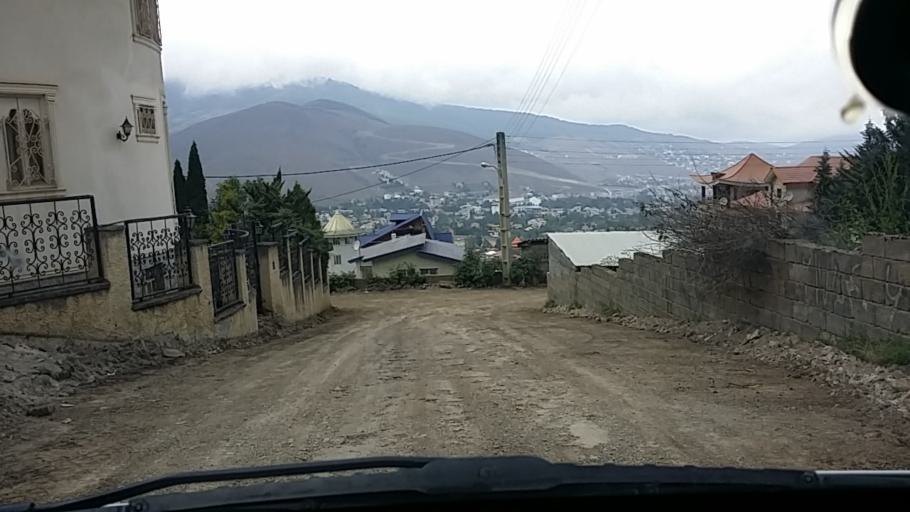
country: IR
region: Mazandaran
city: `Abbasabad
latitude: 36.4900
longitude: 51.1669
